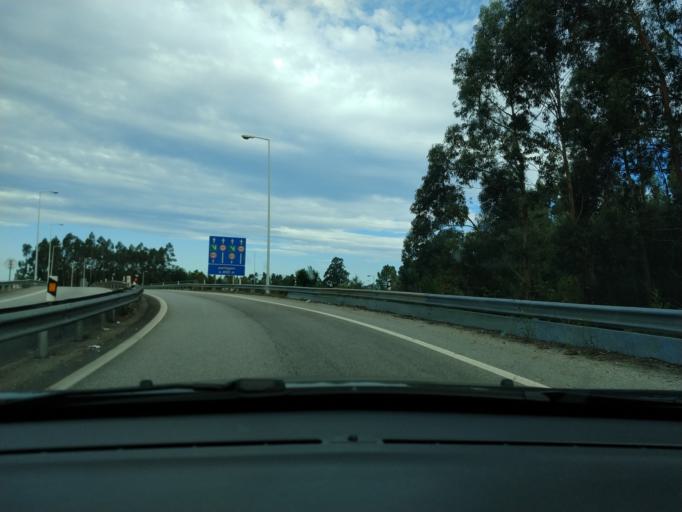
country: PT
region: Aveiro
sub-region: Albergaria-A-Velha
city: Albergaria-a-Velha
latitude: 40.6851
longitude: -8.5242
